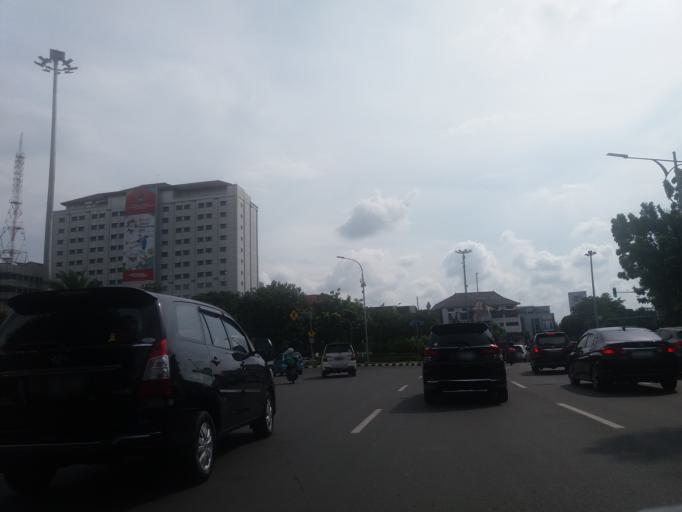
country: ID
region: Jakarta Raya
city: Jakarta
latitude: -6.1715
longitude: 106.8238
